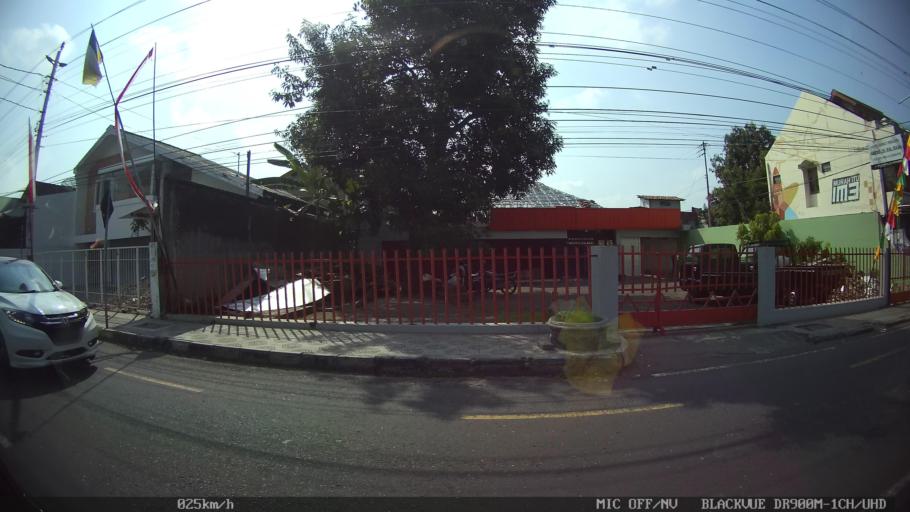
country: ID
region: Daerah Istimewa Yogyakarta
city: Yogyakarta
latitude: -7.8147
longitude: 110.3764
